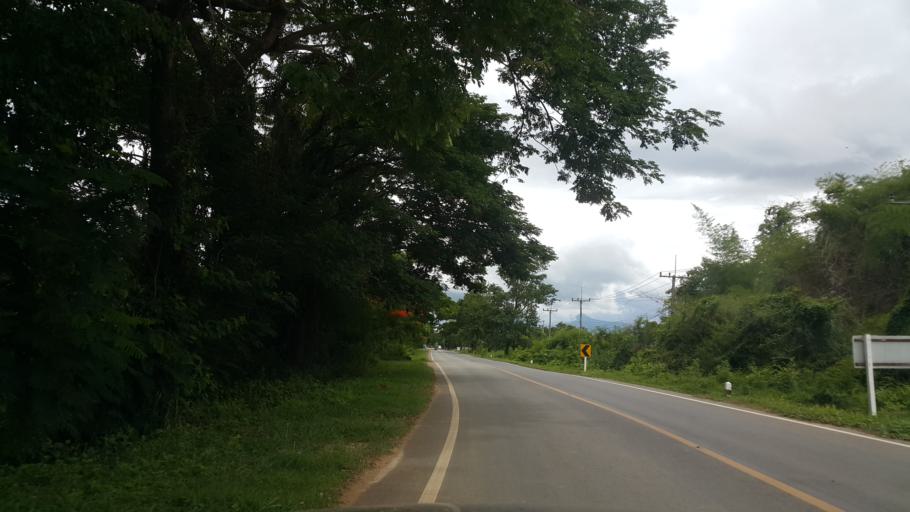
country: TH
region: Sukhothai
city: Ban Na
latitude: 17.0353
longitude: 99.7031
